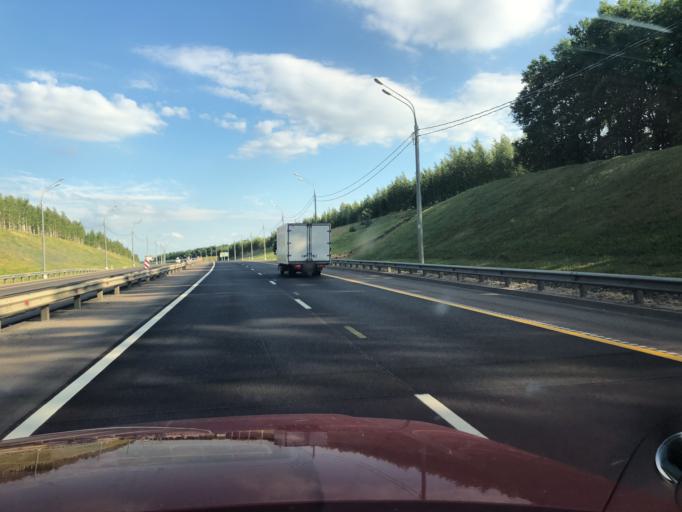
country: RU
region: Lipetsk
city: Zadonsk
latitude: 52.3913
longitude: 38.8637
